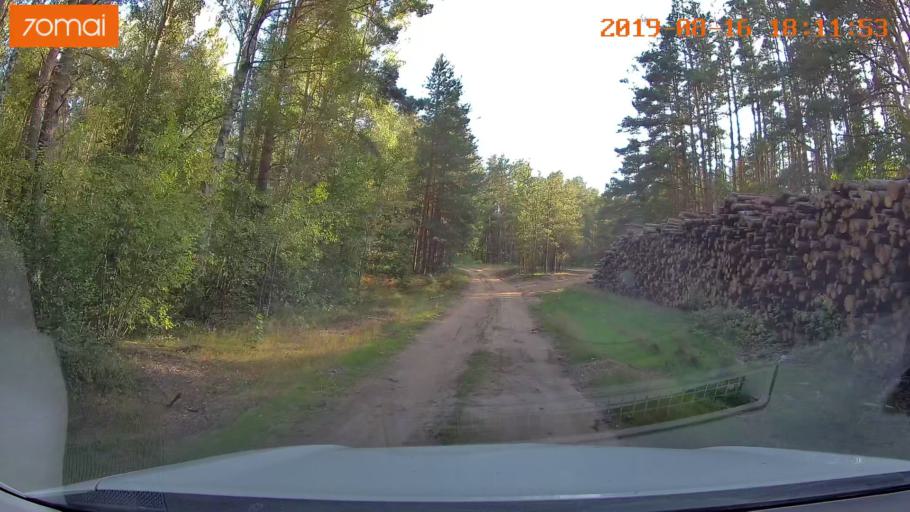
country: BY
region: Mogilev
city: Asipovichy
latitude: 53.2139
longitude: 28.6459
